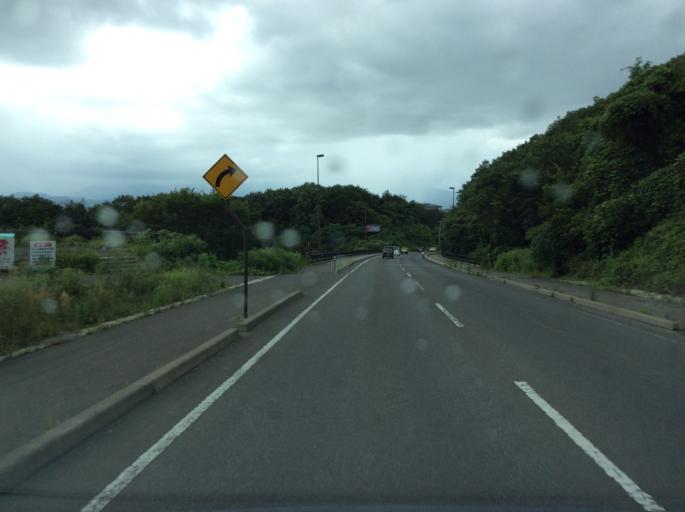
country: JP
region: Fukushima
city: Fukushima-shi
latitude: 37.7234
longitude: 140.4915
